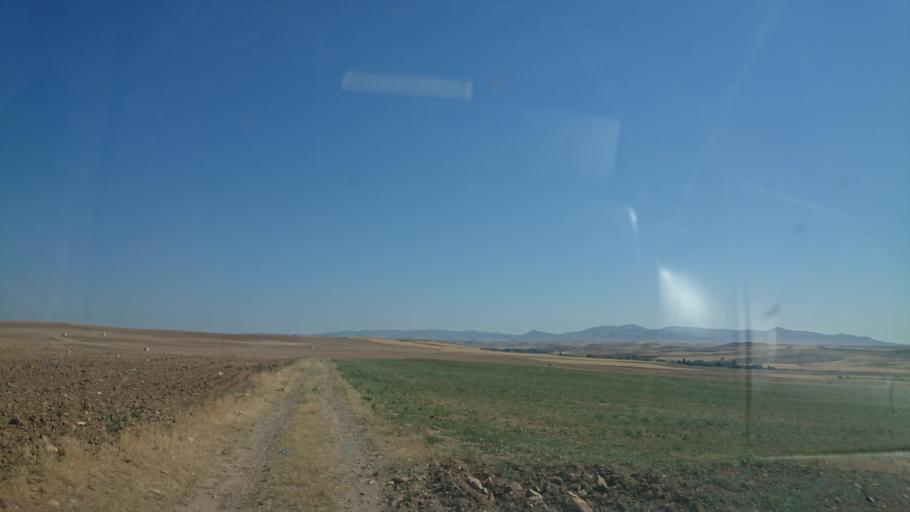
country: TR
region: Aksaray
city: Sariyahsi
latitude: 39.0475
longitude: 33.8903
